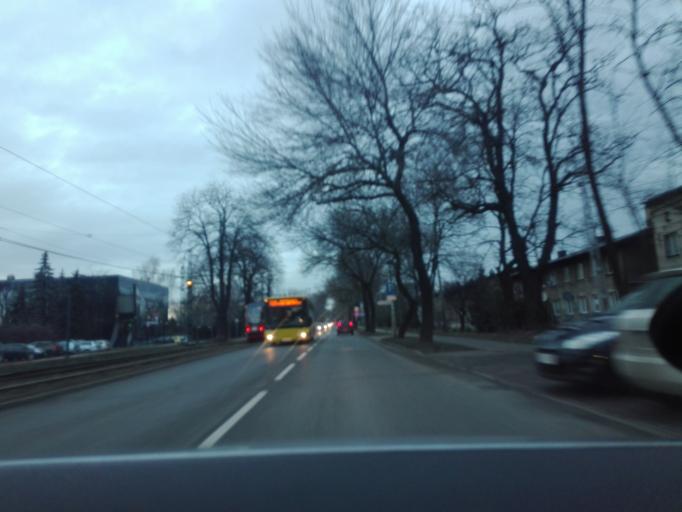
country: PL
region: Silesian Voivodeship
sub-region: Katowice
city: Katowice
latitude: 50.2852
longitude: 19.0182
